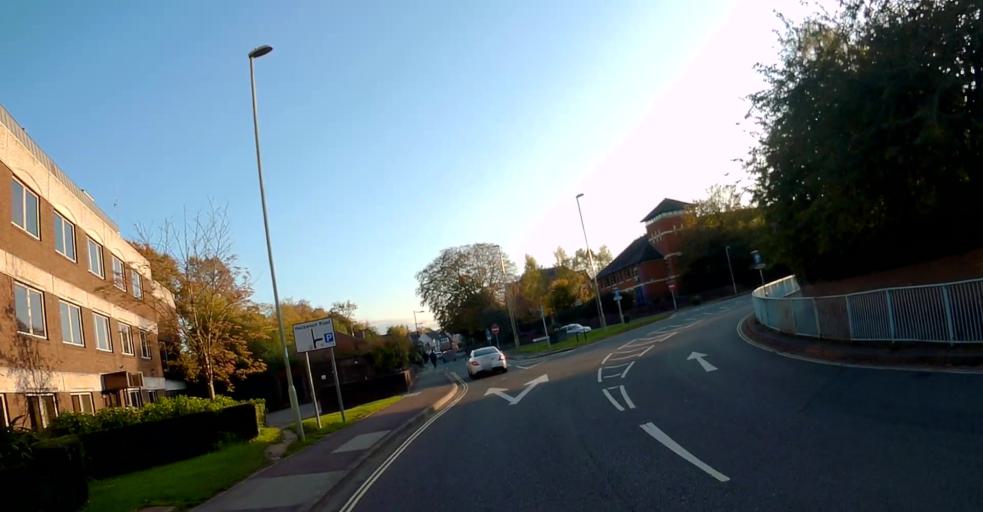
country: GB
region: England
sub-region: Hampshire
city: Basingstoke
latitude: 51.2622
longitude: -1.0841
